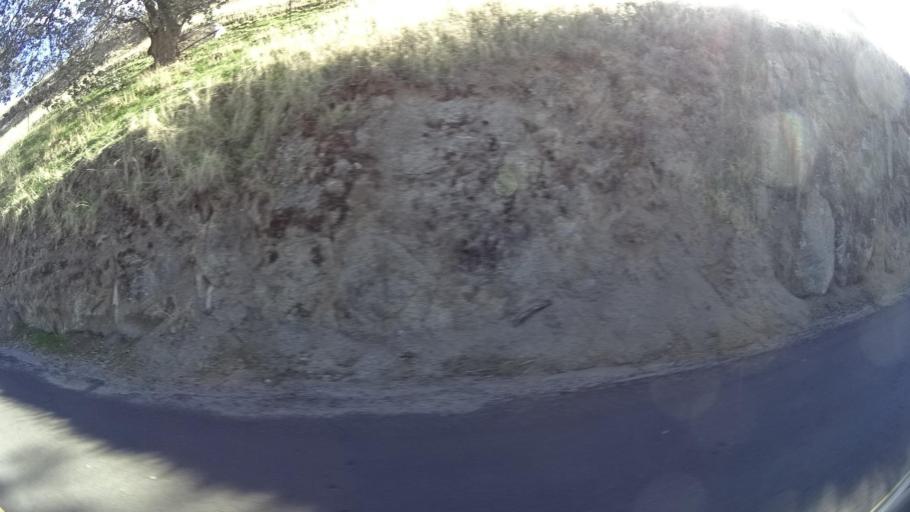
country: US
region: California
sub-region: Tulare County
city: Richgrove
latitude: 35.6942
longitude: -118.8645
